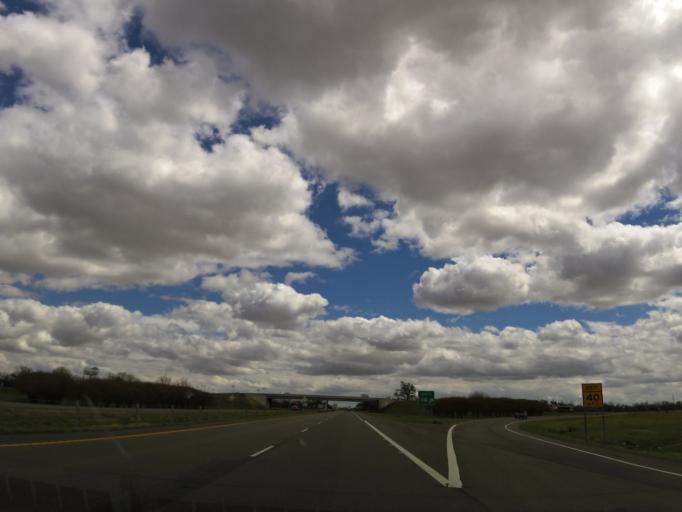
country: US
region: Arkansas
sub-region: Poinsett County
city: Marked Tree
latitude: 35.5272
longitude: -90.4336
